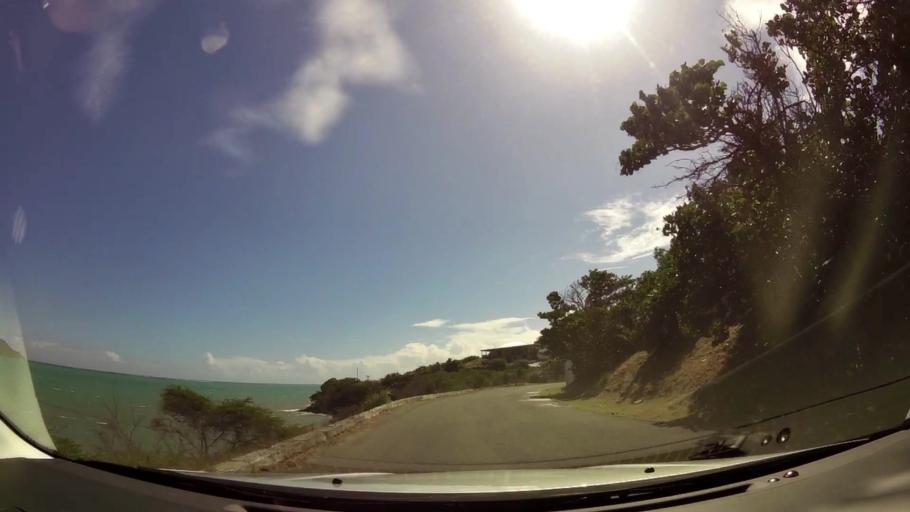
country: AG
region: Saint Paul
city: Falmouth
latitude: 17.0335
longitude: -61.7418
